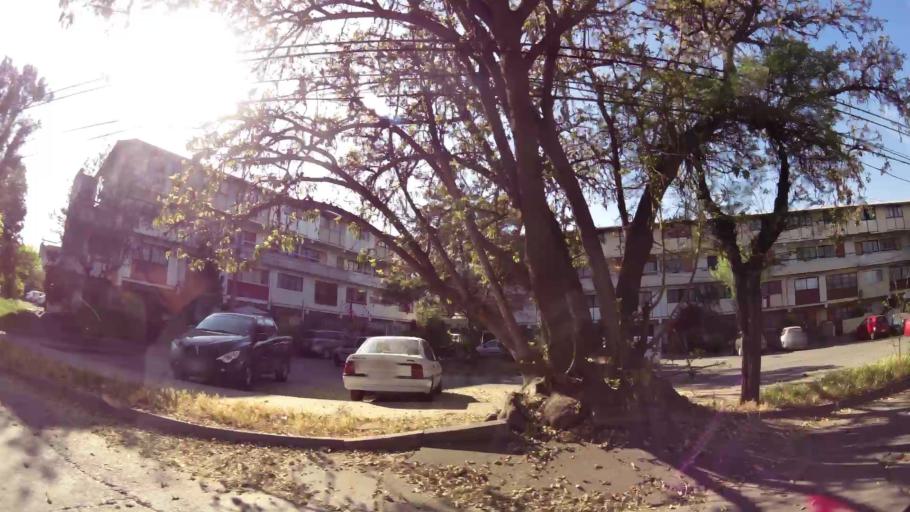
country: CL
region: Santiago Metropolitan
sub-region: Provincia de Santiago
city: Villa Presidente Frei, Nunoa, Santiago, Chile
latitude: -33.4569
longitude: -70.5527
